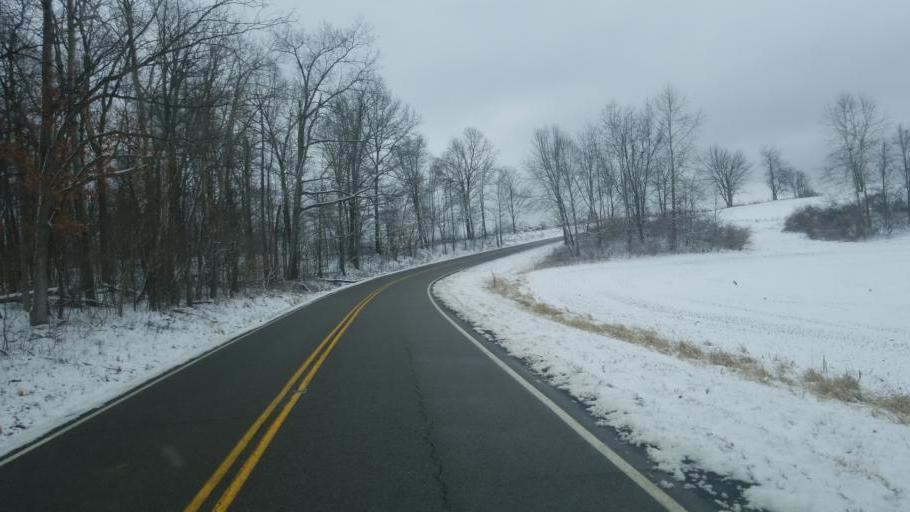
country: US
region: Ohio
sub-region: Knox County
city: Oak Hill
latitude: 40.3916
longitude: -82.1256
